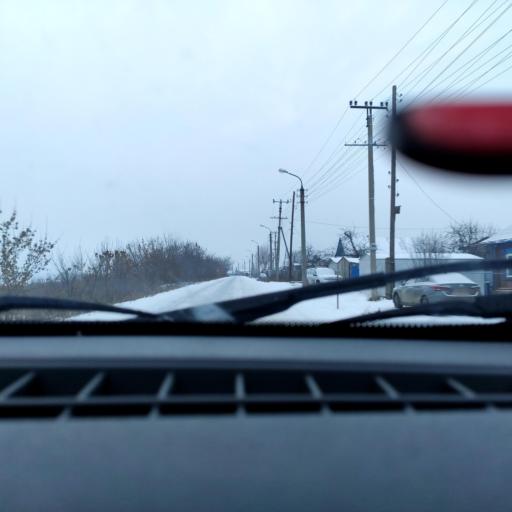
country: RU
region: Bashkortostan
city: Blagoveshchensk
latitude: 54.8912
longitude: 56.0333
